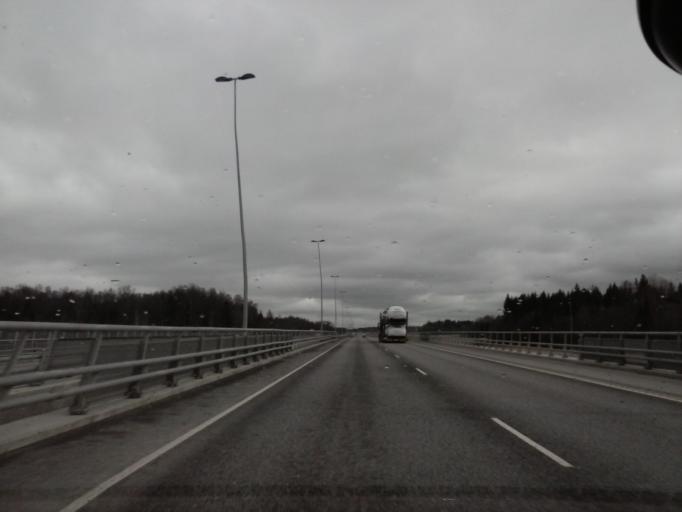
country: EE
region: Harju
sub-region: Rae vald
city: Vaida
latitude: 59.2206
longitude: 25.0347
